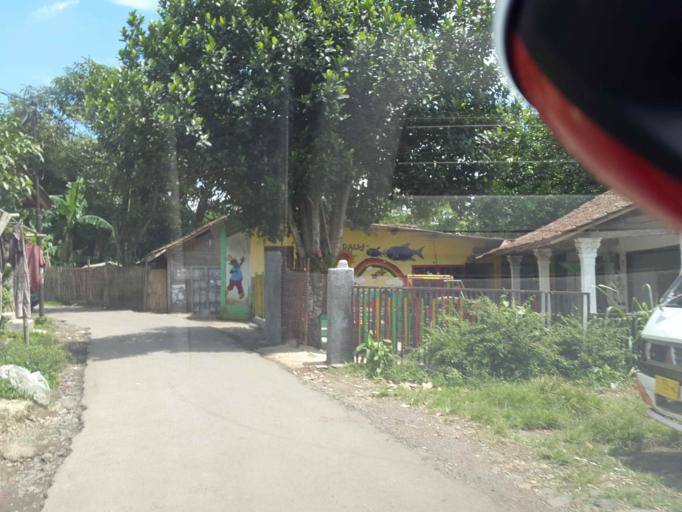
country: ID
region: West Java
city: Sukabumi
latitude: -6.9053
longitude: 106.9407
